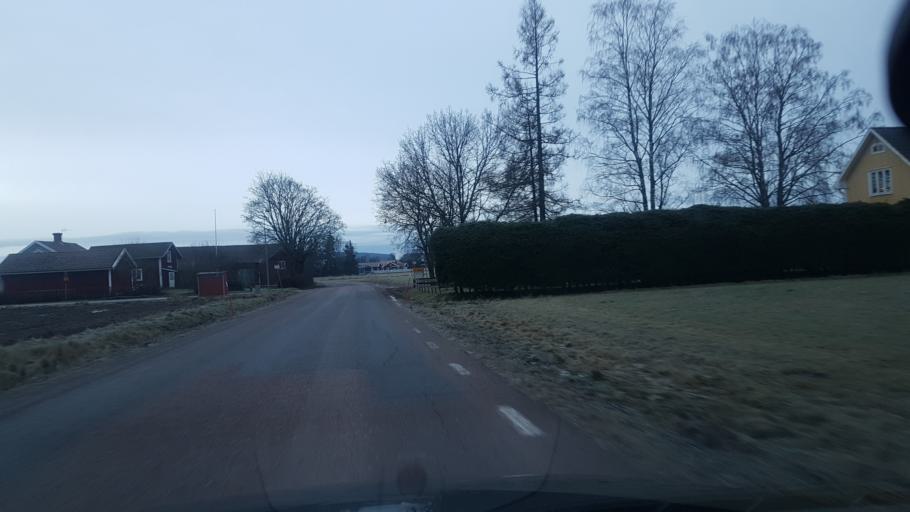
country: SE
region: Dalarna
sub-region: Saters Kommun
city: Saeter
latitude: 60.4288
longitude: 15.6567
